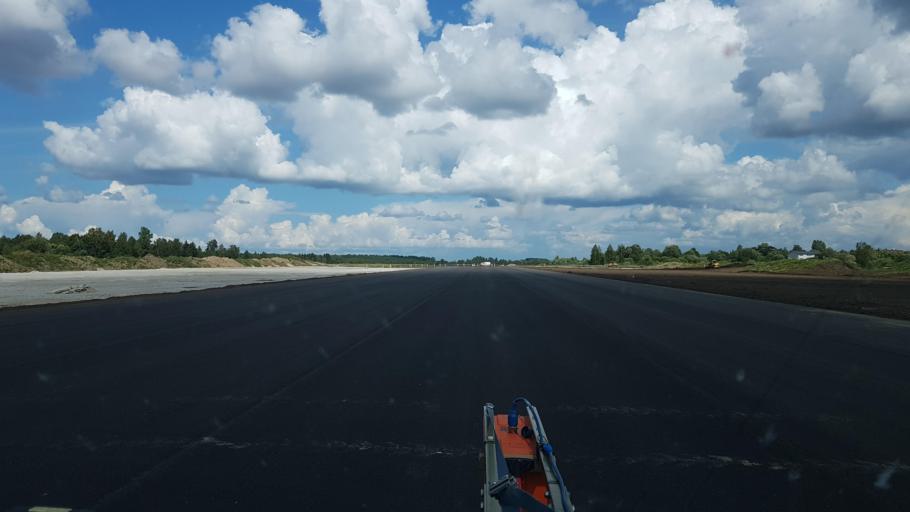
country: EE
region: Paernumaa
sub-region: Sauga vald
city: Sauga
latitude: 58.4255
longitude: 24.4819
